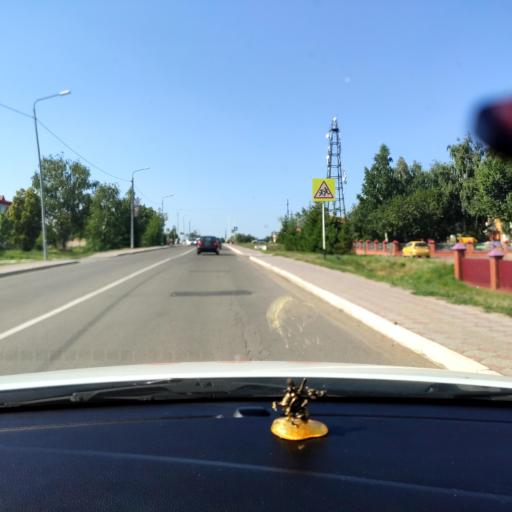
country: RU
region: Tatarstan
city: Laishevo
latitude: 55.4056
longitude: 49.5411
